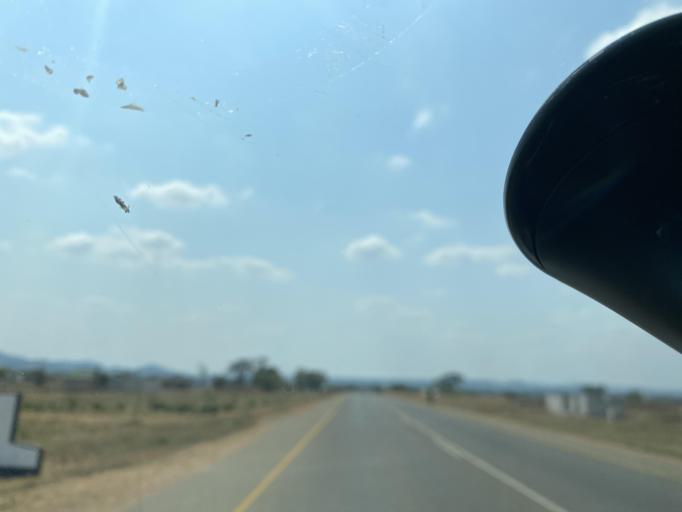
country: ZM
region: Lusaka
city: Chongwe
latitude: -15.5750
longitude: 28.6996
